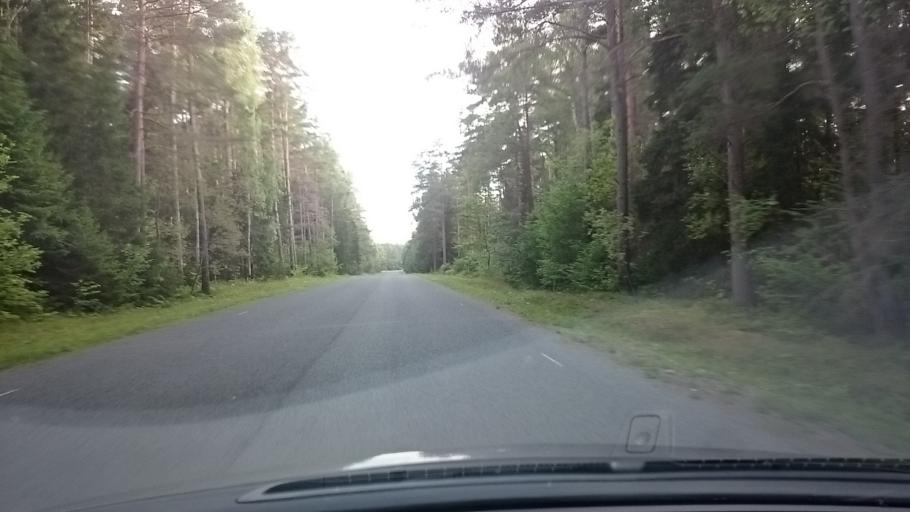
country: EE
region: Saare
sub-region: Kuressaare linn
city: Kuressaare
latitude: 58.4449
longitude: 22.2396
